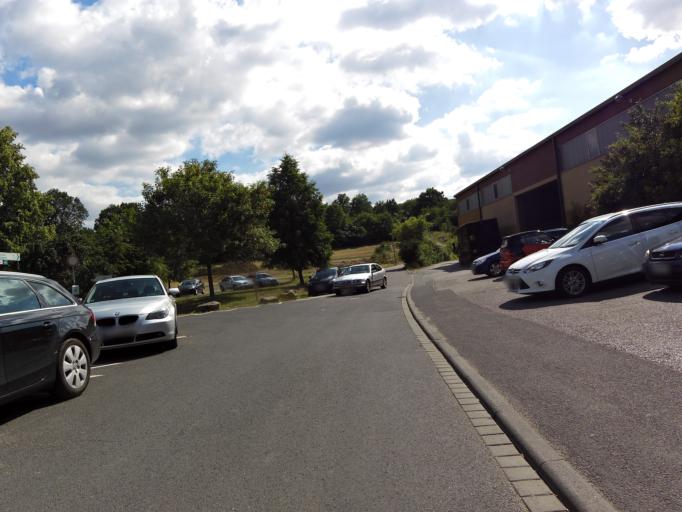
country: DE
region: Bavaria
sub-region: Regierungsbezirk Unterfranken
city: Gerbrunn
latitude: 49.7870
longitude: 9.9955
